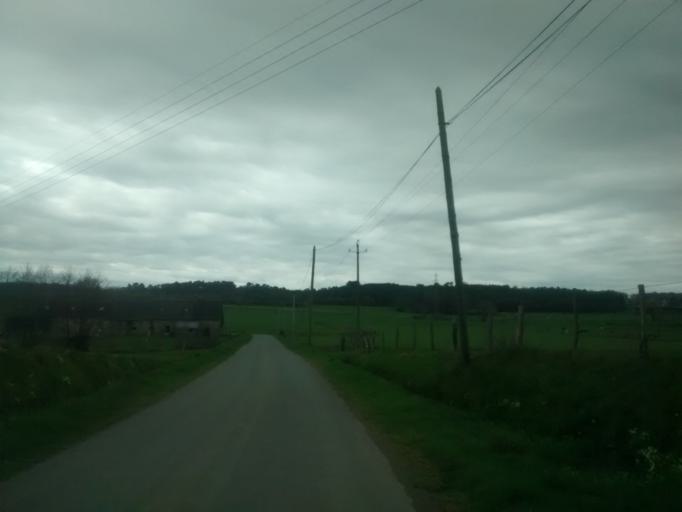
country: FR
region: Brittany
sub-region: Departement d'Ille-et-Vilaine
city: Gosne
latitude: 48.2423
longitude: -1.4751
